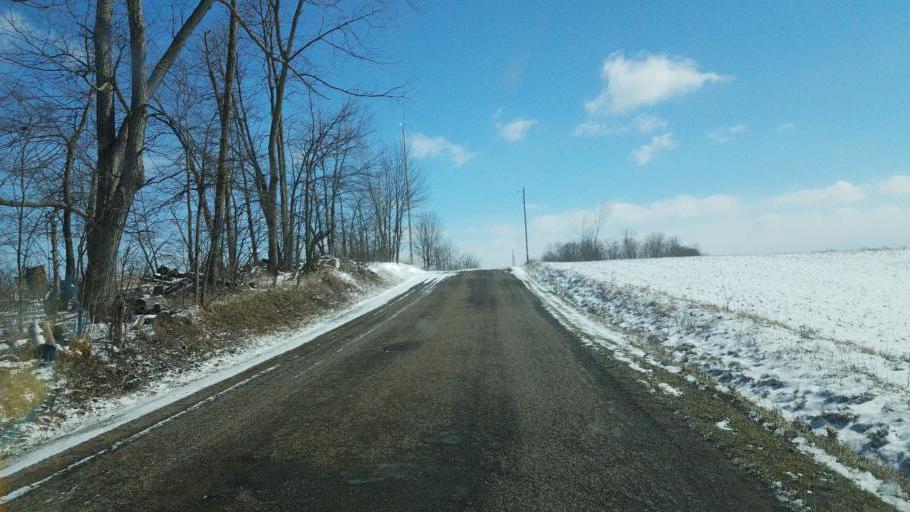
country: US
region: Ohio
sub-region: Morrow County
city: Mount Gilead
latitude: 40.4794
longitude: -82.7080
